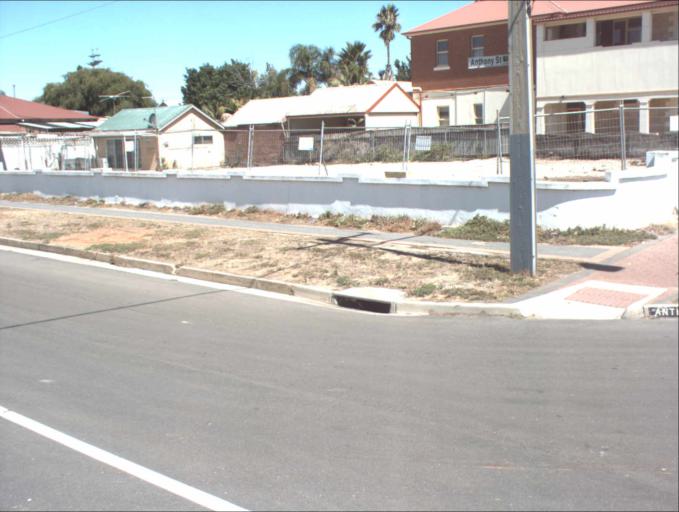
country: AU
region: South Australia
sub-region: Port Adelaide Enfield
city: Birkenhead
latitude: -34.8277
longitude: 138.4851
